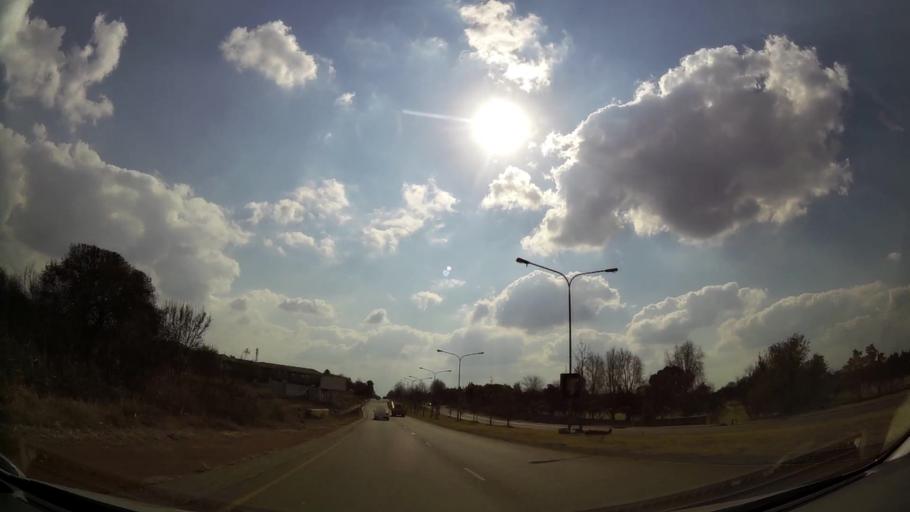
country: ZA
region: Gauteng
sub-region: City of Tshwane Metropolitan Municipality
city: Centurion
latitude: -25.8801
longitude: 28.2026
